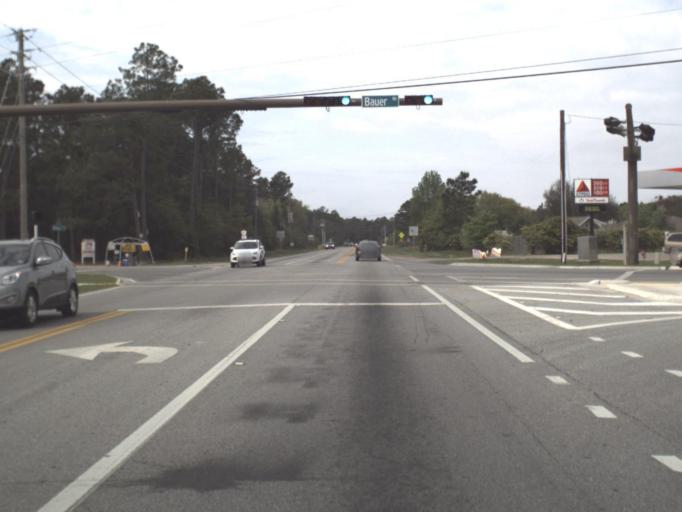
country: US
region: Florida
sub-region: Escambia County
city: Myrtle Grove
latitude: 30.3411
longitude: -87.4028
